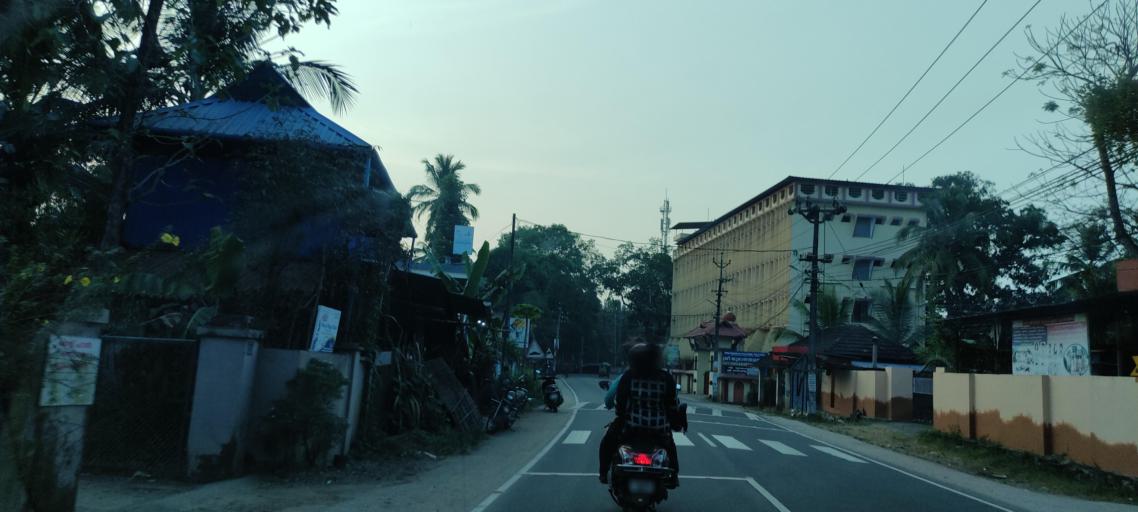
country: IN
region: Kerala
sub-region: Alappuzha
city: Mavelikara
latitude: 9.2684
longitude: 76.5391
